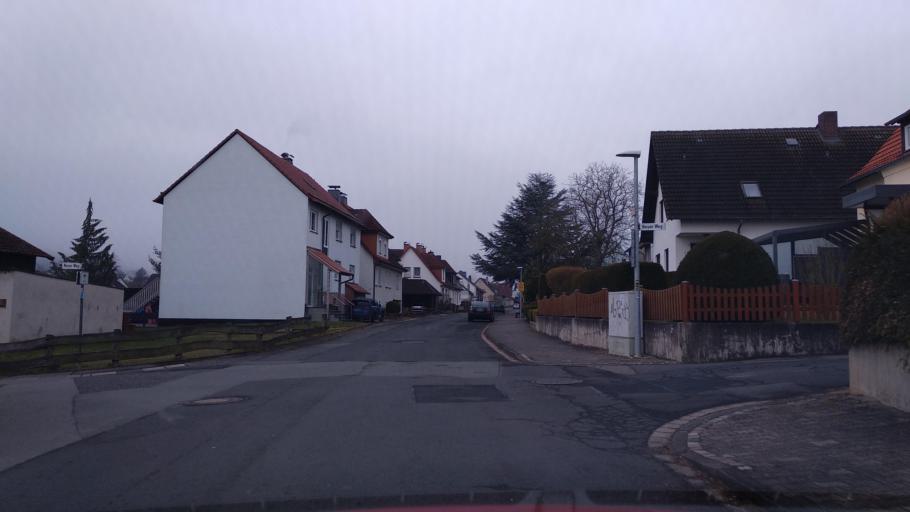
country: DE
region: Hesse
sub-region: Regierungsbezirk Kassel
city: Calden
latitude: 51.3661
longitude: 9.3879
